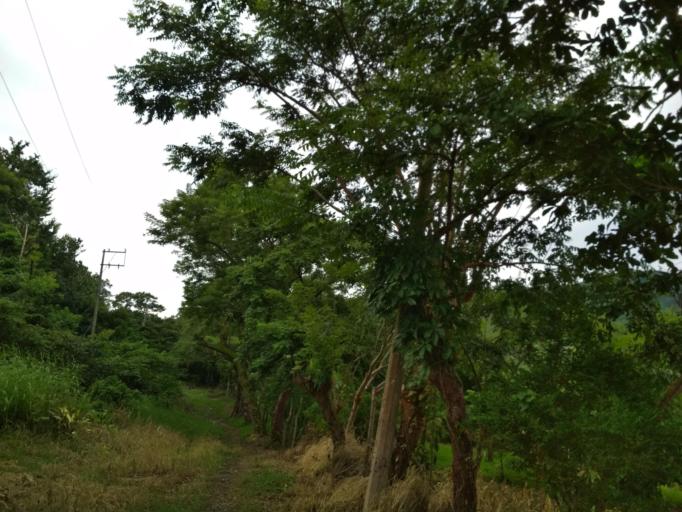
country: MX
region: Veracruz
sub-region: San Andres Tuxtla
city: Los Pinos
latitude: 18.4461
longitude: -95.2339
